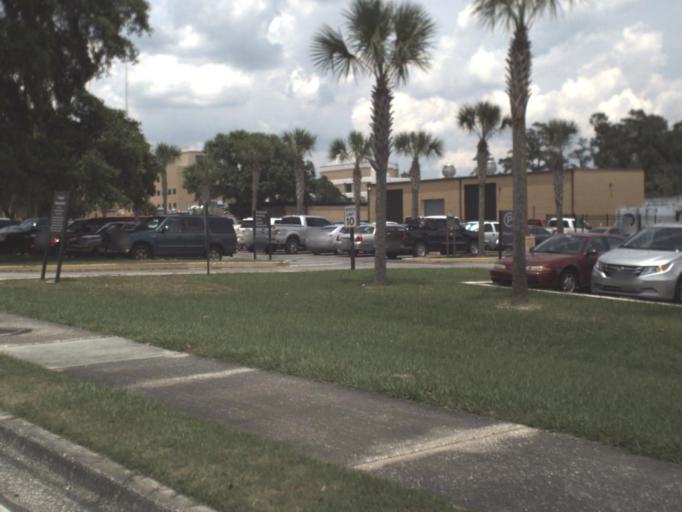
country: US
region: Florida
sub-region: Columbia County
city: Lake City
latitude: 30.1794
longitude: -82.6369
